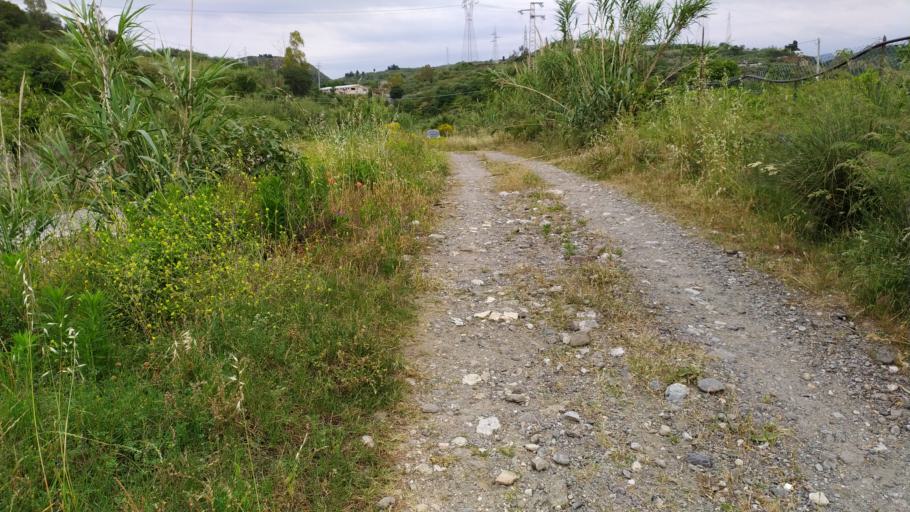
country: IT
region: Sicily
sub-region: Messina
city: San Filippo del Mela
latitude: 38.1712
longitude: 15.2795
